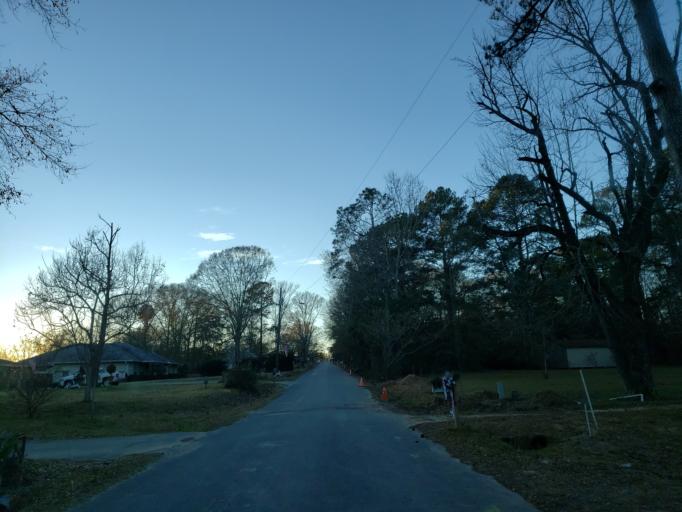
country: US
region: Mississippi
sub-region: Covington County
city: Collins
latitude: 31.5636
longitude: -89.4899
